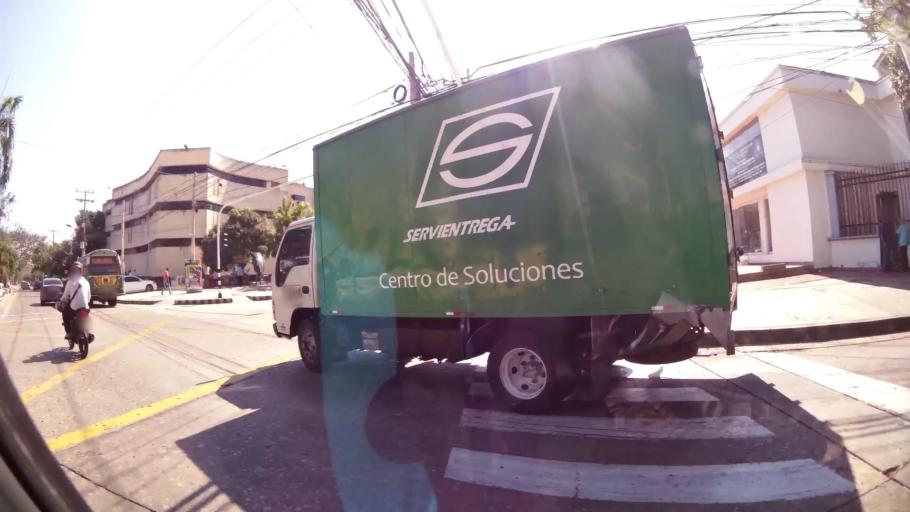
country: CO
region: Atlantico
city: Barranquilla
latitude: 10.9951
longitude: -74.7960
